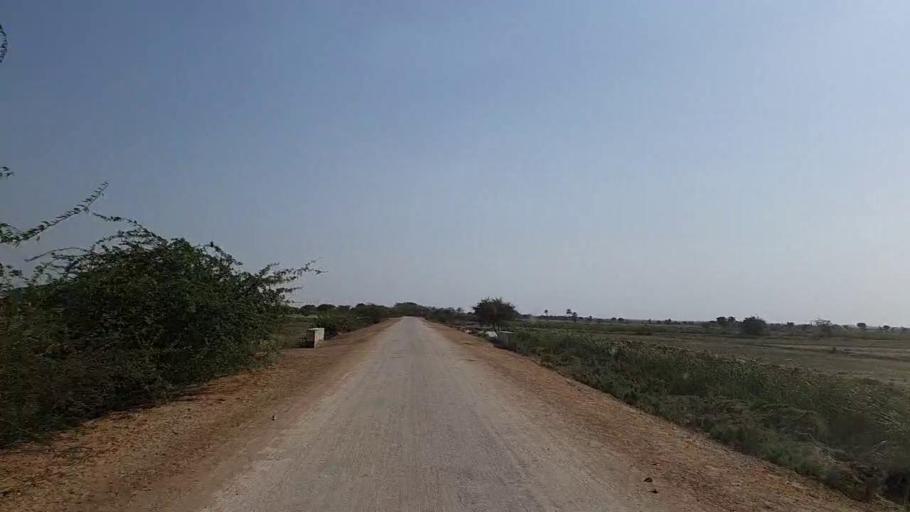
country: PK
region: Sindh
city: Daro Mehar
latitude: 24.7726
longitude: 68.1813
